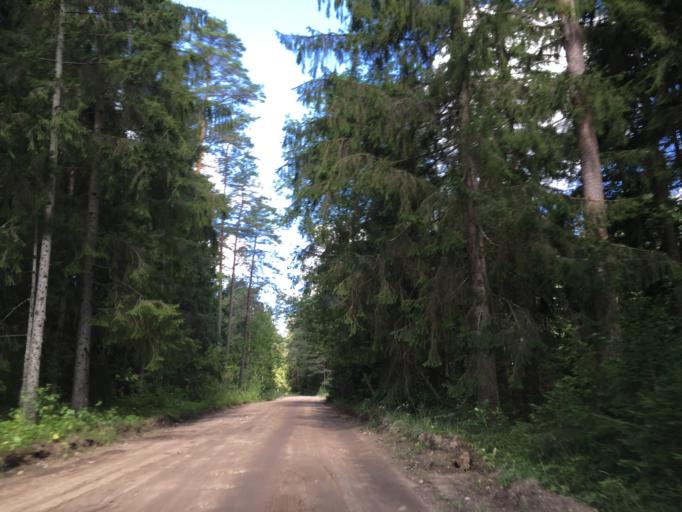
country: LV
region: Garkalne
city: Garkalne
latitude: 56.9725
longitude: 24.4630
